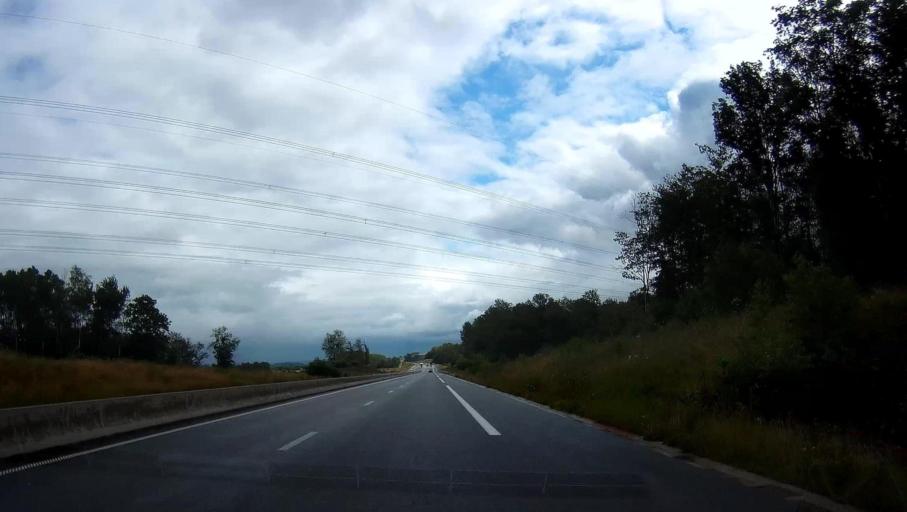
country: FR
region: Champagne-Ardenne
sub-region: Departement des Ardennes
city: Rimogne
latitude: 49.7887
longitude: 4.5624
